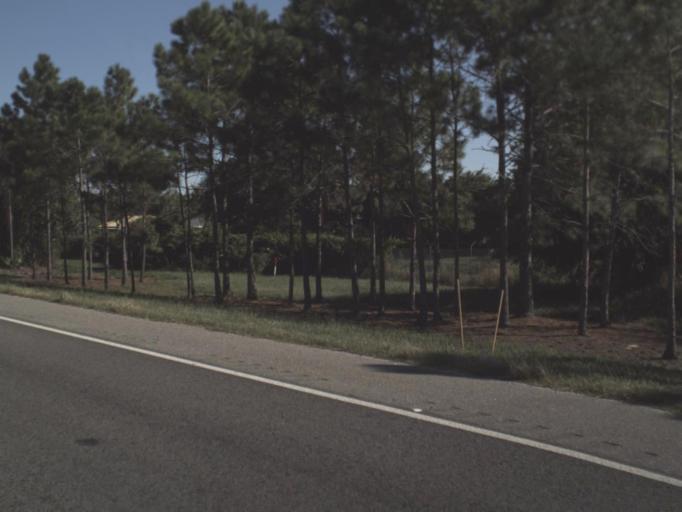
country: US
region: Florida
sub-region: Orange County
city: Williamsburg
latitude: 28.4210
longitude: -81.4533
